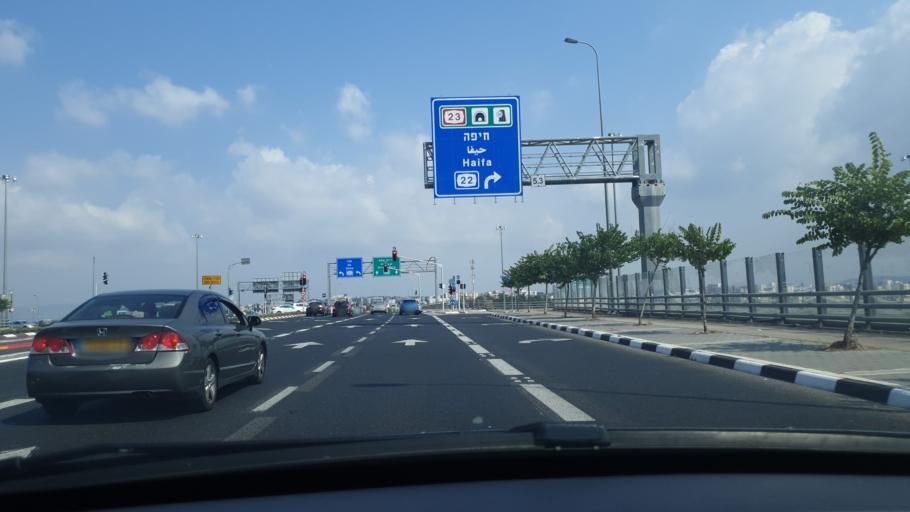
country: IL
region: Haifa
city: Qiryat Bialik
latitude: 32.8149
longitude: 35.0889
